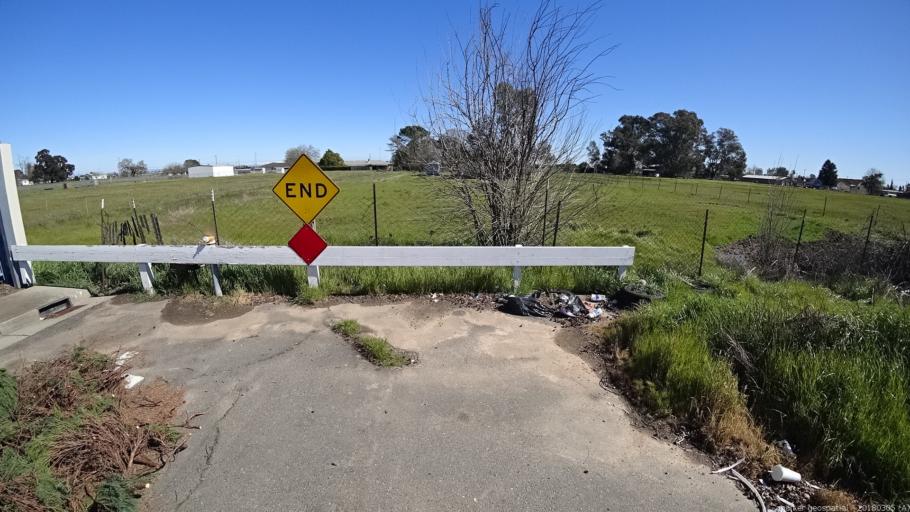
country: US
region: California
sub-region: Sacramento County
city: Florin
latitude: 38.4998
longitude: -121.3814
